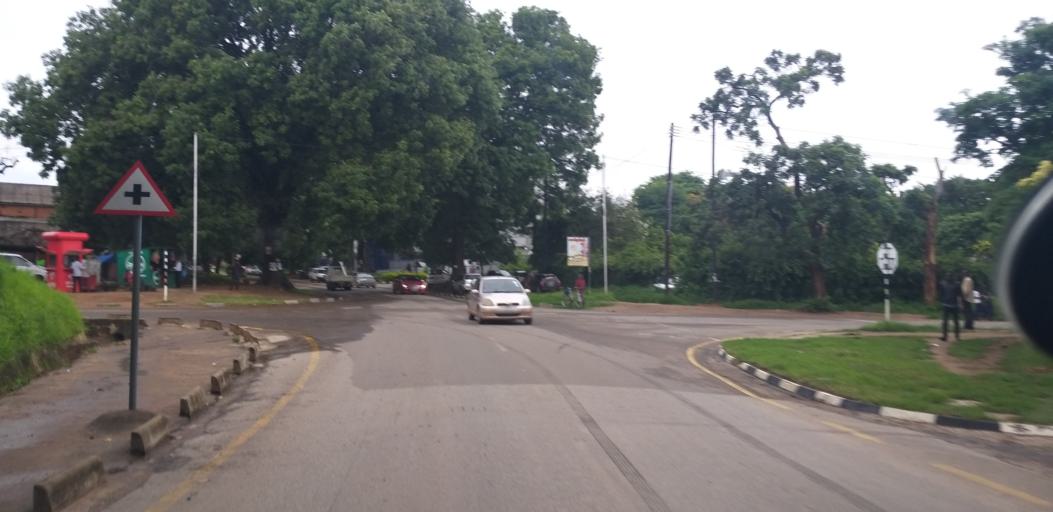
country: ZM
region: Lusaka
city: Lusaka
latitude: -15.4196
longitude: 28.2993
